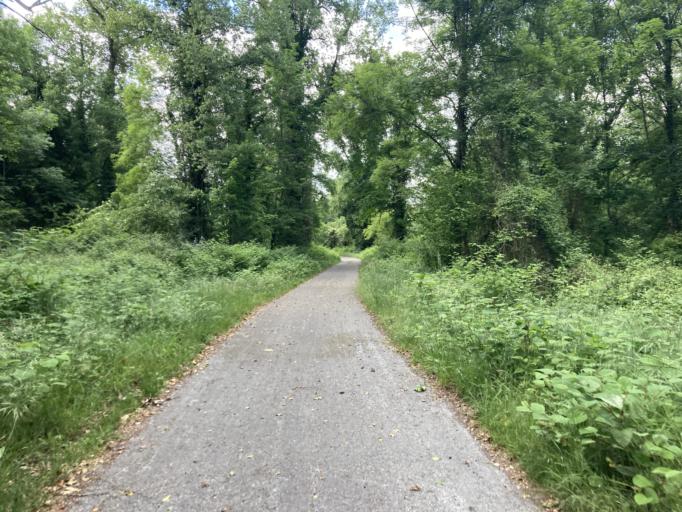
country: FR
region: Aquitaine
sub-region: Departement des Pyrenees-Atlantiques
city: Arbus
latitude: 43.3475
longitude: -0.5127
